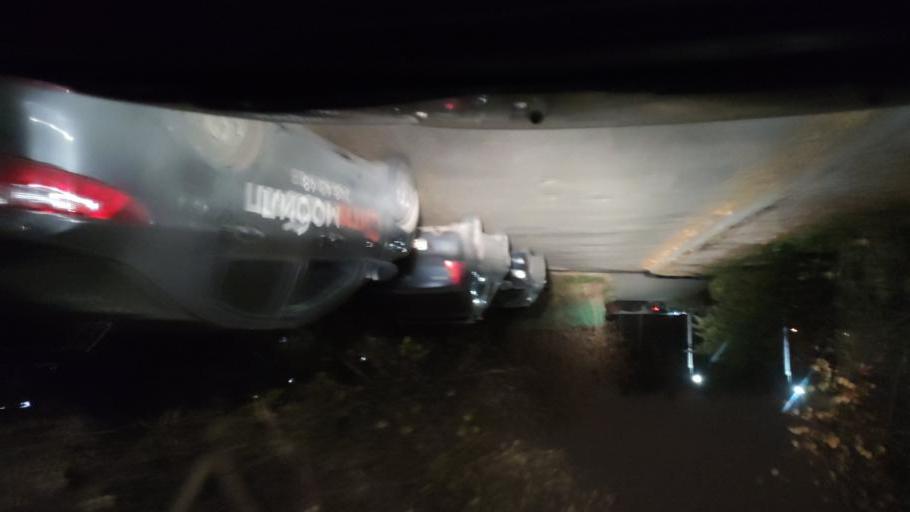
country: RU
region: Perm
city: Perm
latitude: 57.9872
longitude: 56.2321
